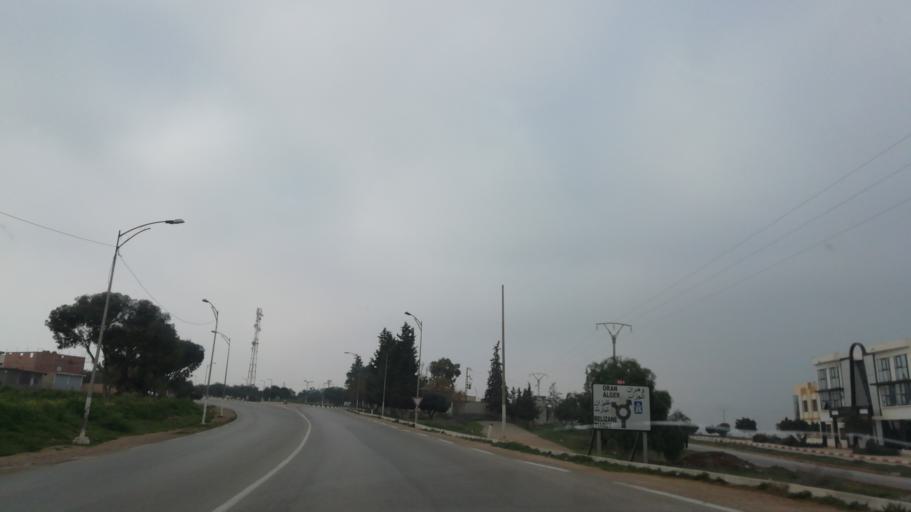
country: DZ
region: Relizane
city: Djidiouia
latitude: 35.8923
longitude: 0.7365
